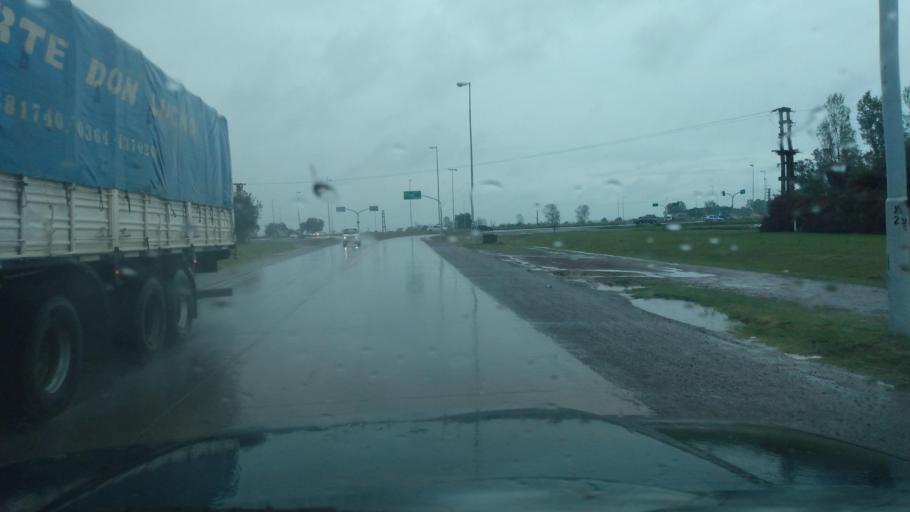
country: AR
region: Buenos Aires
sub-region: Partido de Campana
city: Campana
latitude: -34.2015
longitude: -58.9578
